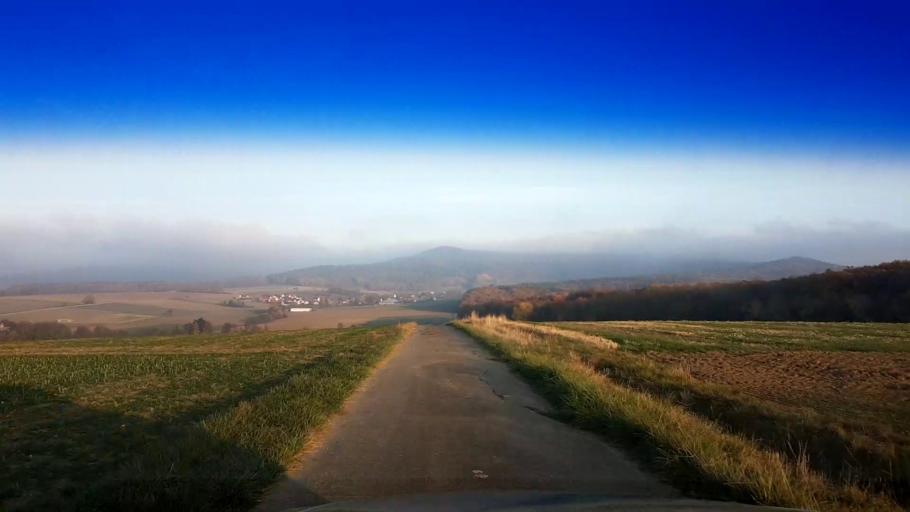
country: DE
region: Bavaria
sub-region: Upper Franconia
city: Memmelsdorf
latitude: 49.9359
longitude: 10.9881
